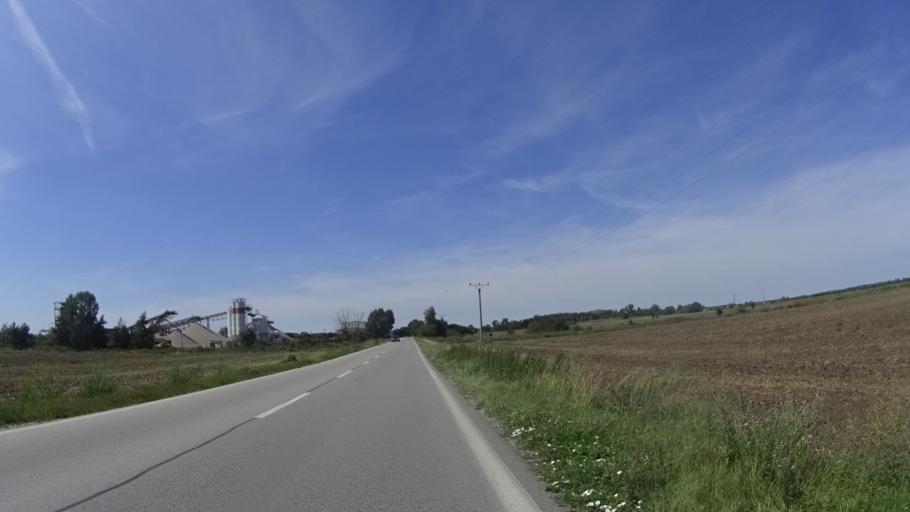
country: AT
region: Lower Austria
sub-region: Politischer Bezirk Ganserndorf
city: Marchegg
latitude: 48.3136
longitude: 16.9285
